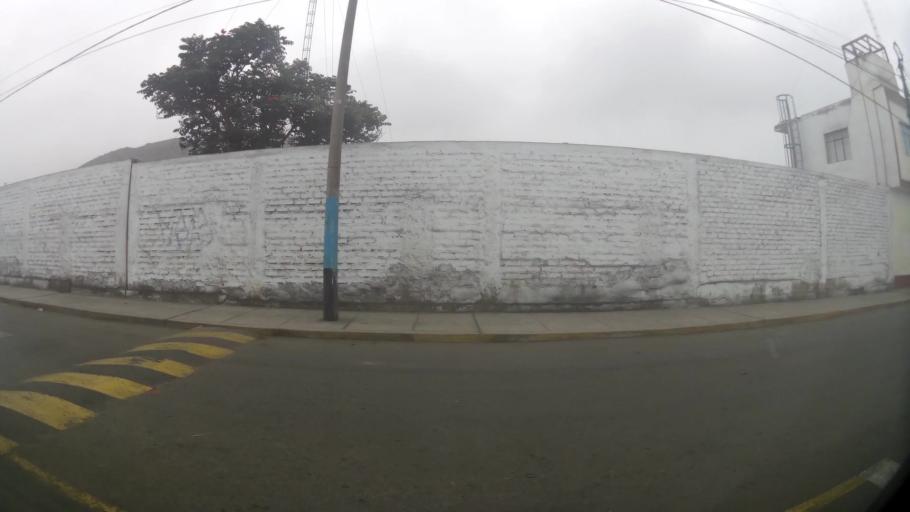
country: PE
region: Lima
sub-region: Provincia de Huaral
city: Chancay
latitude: -11.5833
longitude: -77.2698
